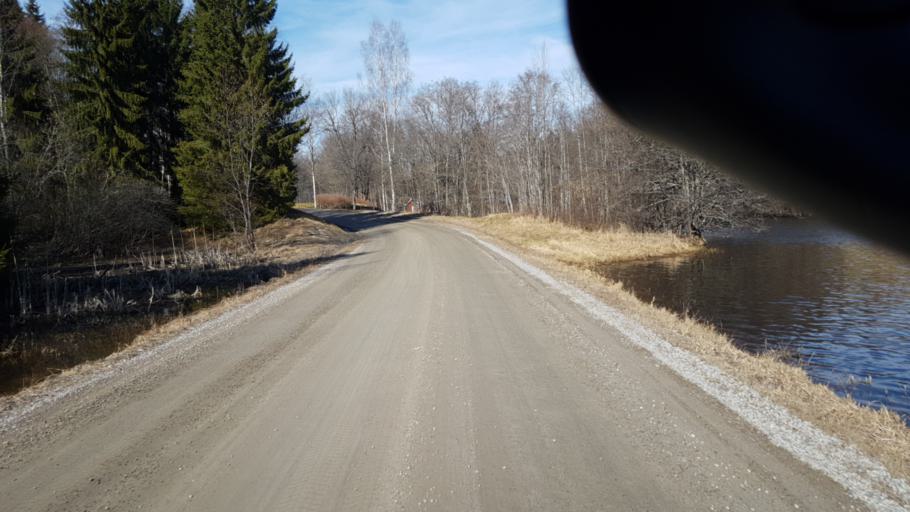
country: SE
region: Vaermland
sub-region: Sunne Kommun
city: Sunne
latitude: 59.6926
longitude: 12.8879
